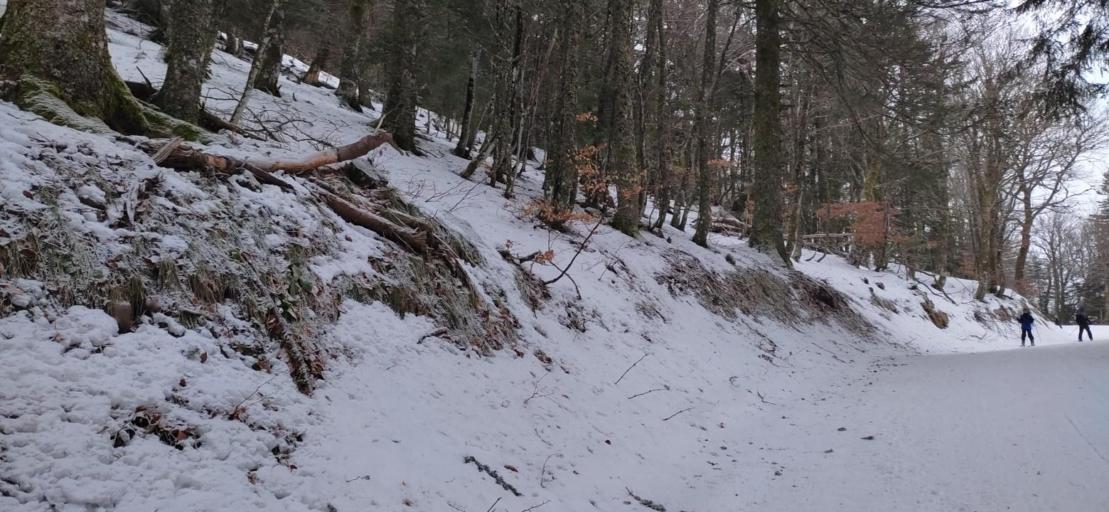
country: FR
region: Auvergne
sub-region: Departement du Puy-de-Dome
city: Mont-Dore
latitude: 45.5431
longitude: 2.8185
